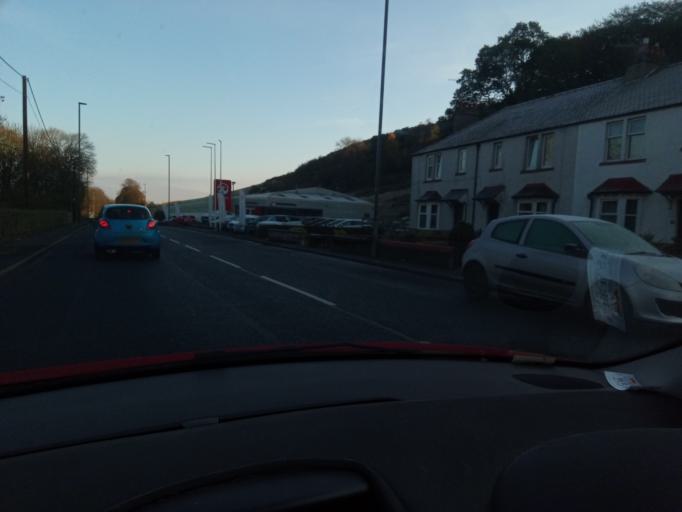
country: GB
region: Scotland
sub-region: The Scottish Borders
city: Hawick
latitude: 55.4325
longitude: -2.7606
